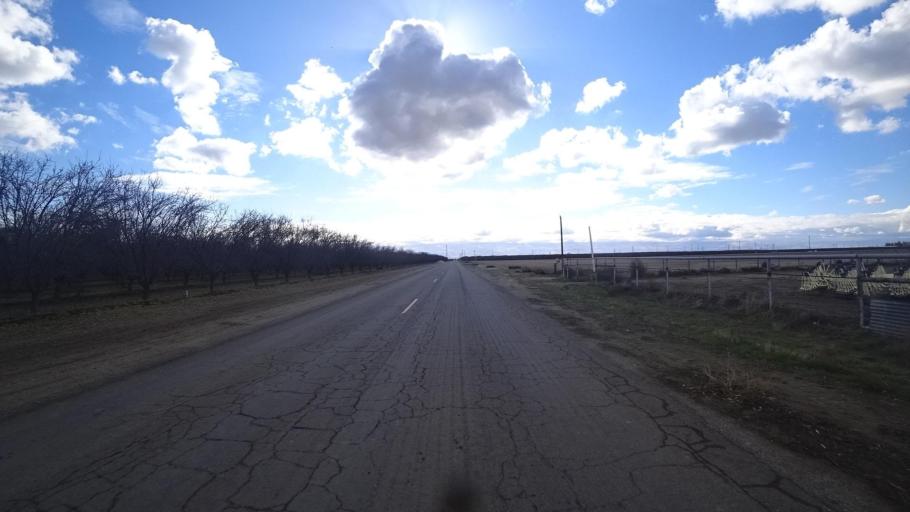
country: US
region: California
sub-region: Kern County
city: Greenfield
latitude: 35.2161
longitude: -119.0923
